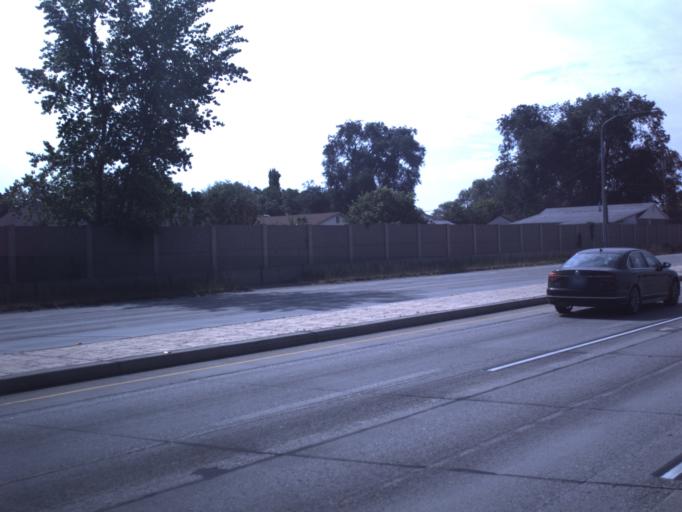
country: US
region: Utah
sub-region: Salt Lake County
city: West Valley City
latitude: 40.7025
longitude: -111.9802
